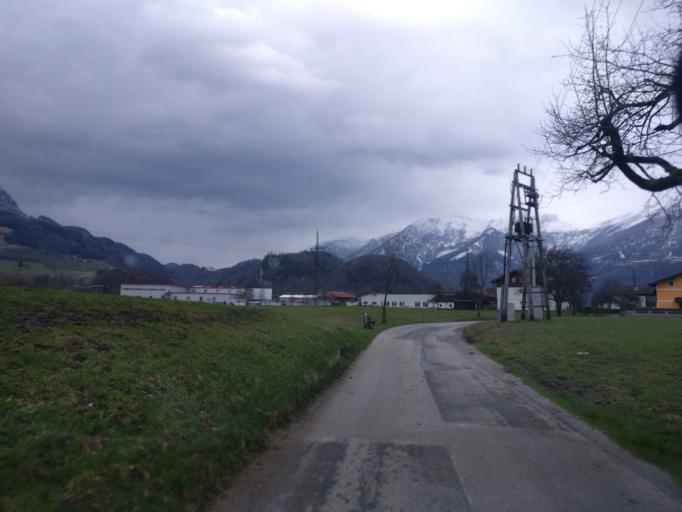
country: AT
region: Salzburg
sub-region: Politischer Bezirk Hallein
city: Golling an der Salzach
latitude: 47.6109
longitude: 13.1584
